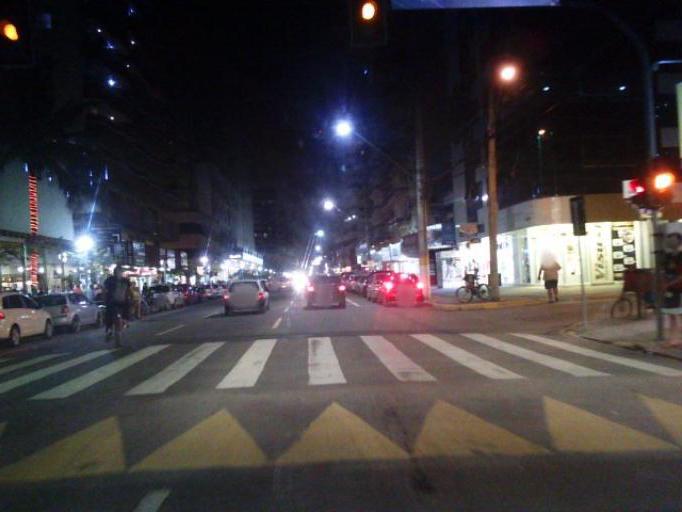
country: BR
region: Santa Catarina
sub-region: Itapema
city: Itapema
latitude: -27.1288
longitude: -48.6015
